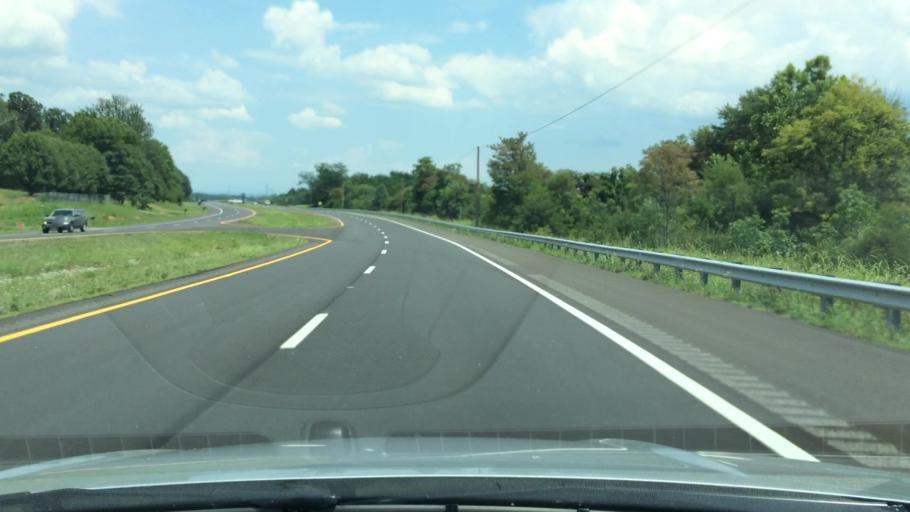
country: US
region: Tennessee
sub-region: Hamblen County
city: Morristown
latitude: 36.1833
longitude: -83.2532
